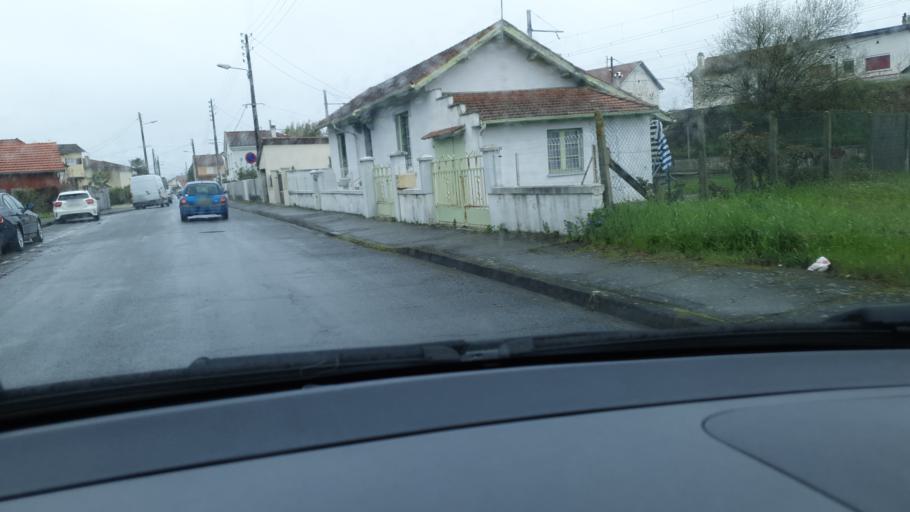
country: FR
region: Midi-Pyrenees
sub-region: Departement des Hautes-Pyrenees
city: Tarbes
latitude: 43.2407
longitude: 0.0577
